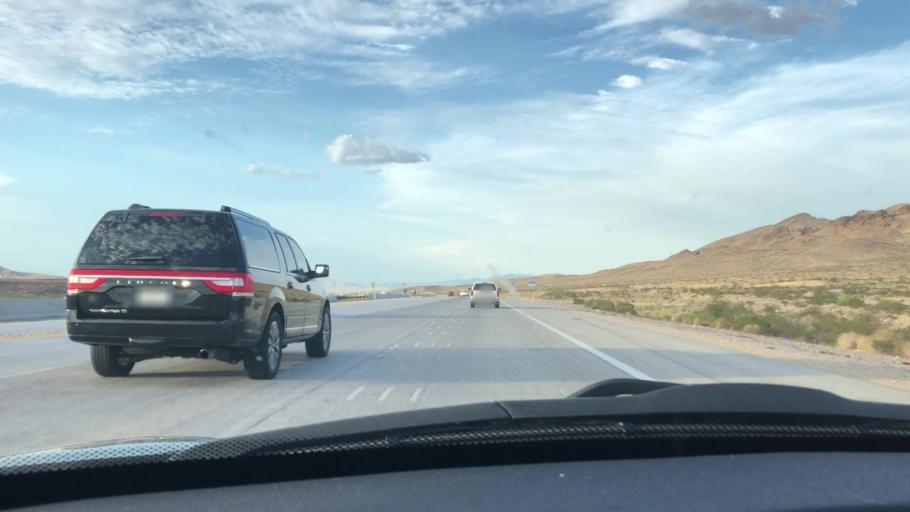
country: US
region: Nevada
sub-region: Clark County
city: Enterprise
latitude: 35.8853
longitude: -115.2262
